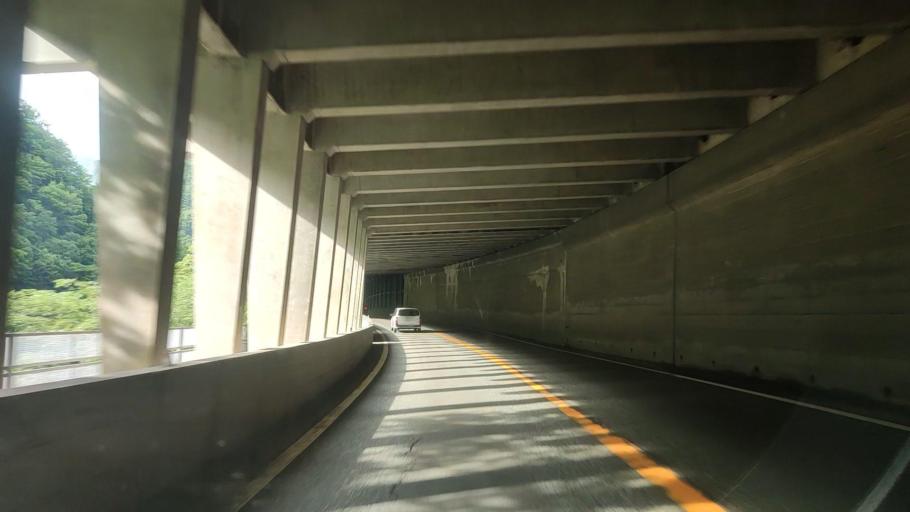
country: JP
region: Toyama
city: Yatsuomachi-higashikumisaka
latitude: 36.3768
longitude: 137.2777
